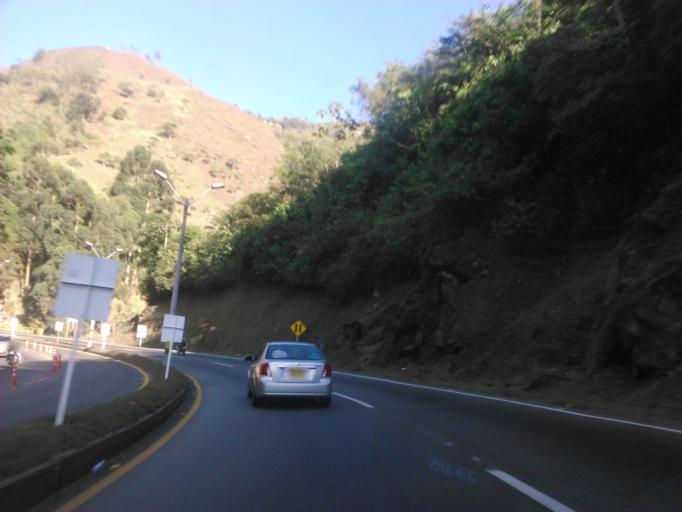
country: CO
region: Antioquia
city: Municipio de Copacabana
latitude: 6.3113
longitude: -75.5049
